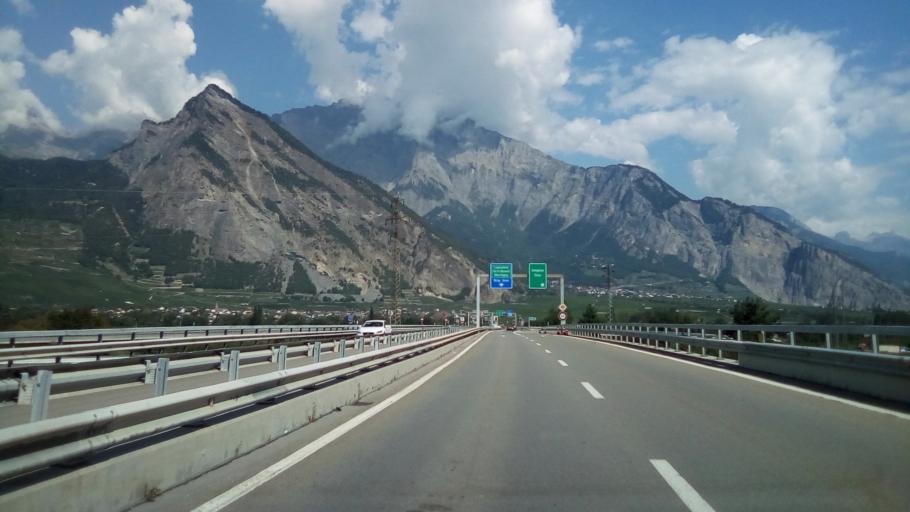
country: CH
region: Valais
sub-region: Martigny District
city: Riddes
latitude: 46.1701
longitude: 7.2144
